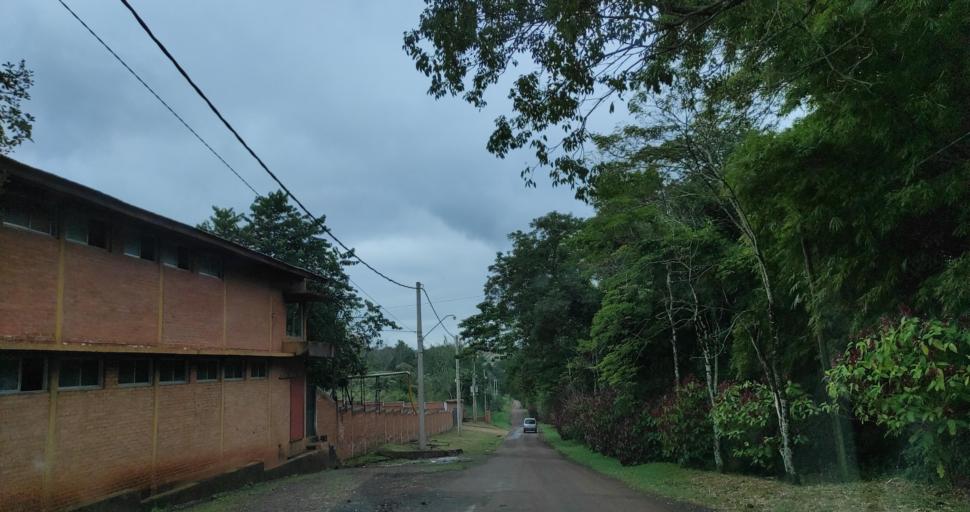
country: AR
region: Misiones
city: Puerto Rico
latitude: -26.7956
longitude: -55.0170
